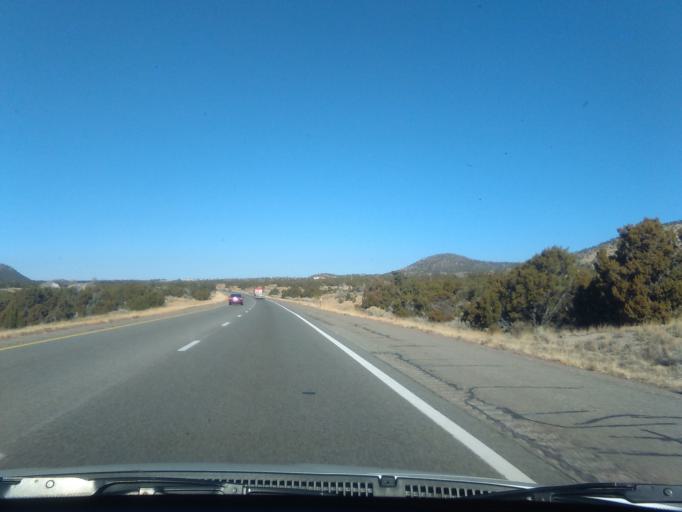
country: US
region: New Mexico
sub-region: Santa Fe County
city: Eldorado at Santa Fe
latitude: 35.5664
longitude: -105.8857
